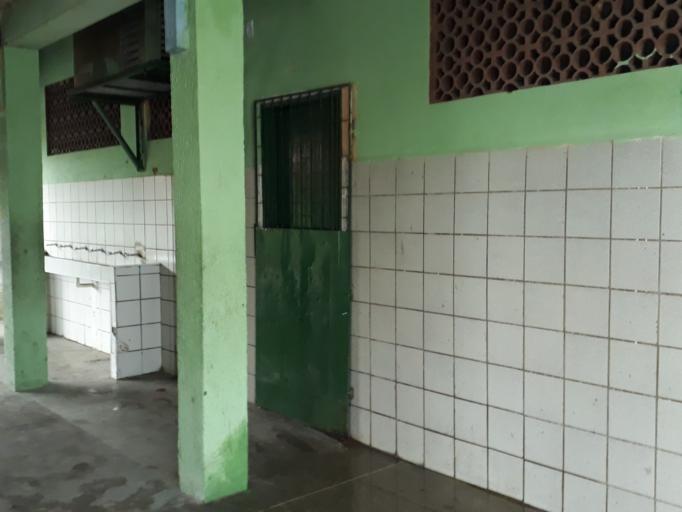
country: BR
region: Ceara
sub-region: Fortaleza
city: Fortaleza
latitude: -3.7232
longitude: -38.5887
